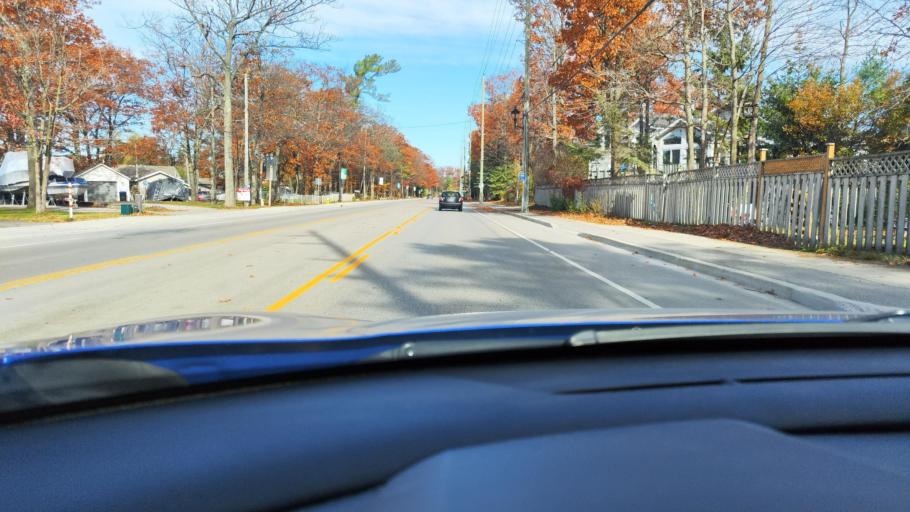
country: CA
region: Ontario
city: Wasaga Beach
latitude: 44.4932
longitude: -80.0440
